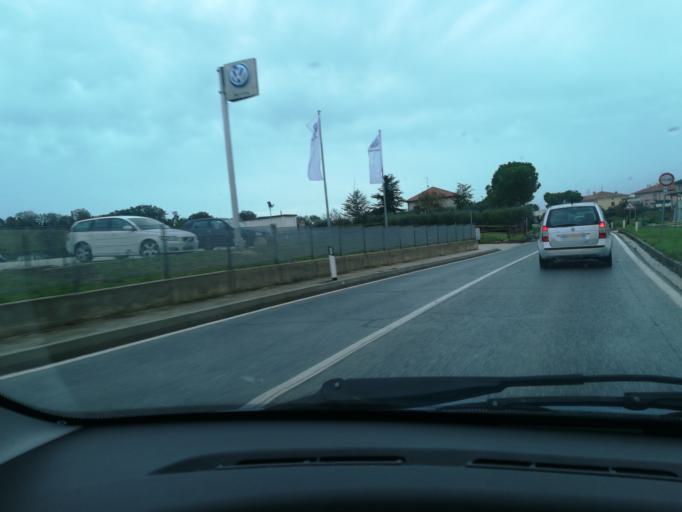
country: IT
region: The Marches
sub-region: Provincia di Macerata
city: Santa Maria Apparente
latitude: 43.2944
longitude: 13.6743
